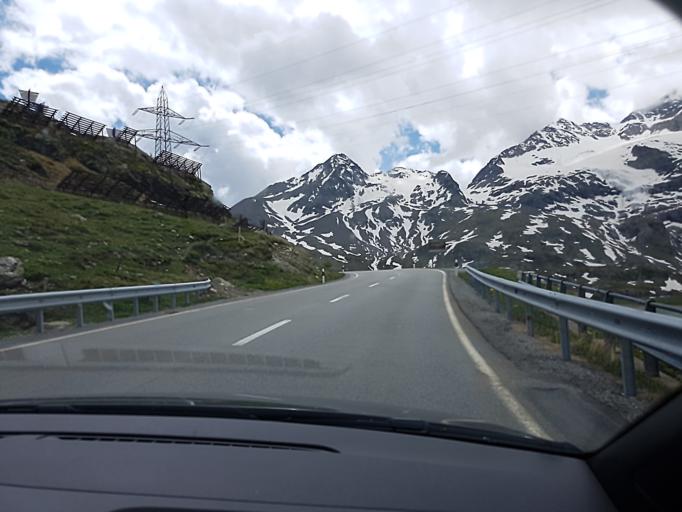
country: CH
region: Grisons
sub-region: Bernina District
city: Poschiavo
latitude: 46.4164
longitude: 10.0211
